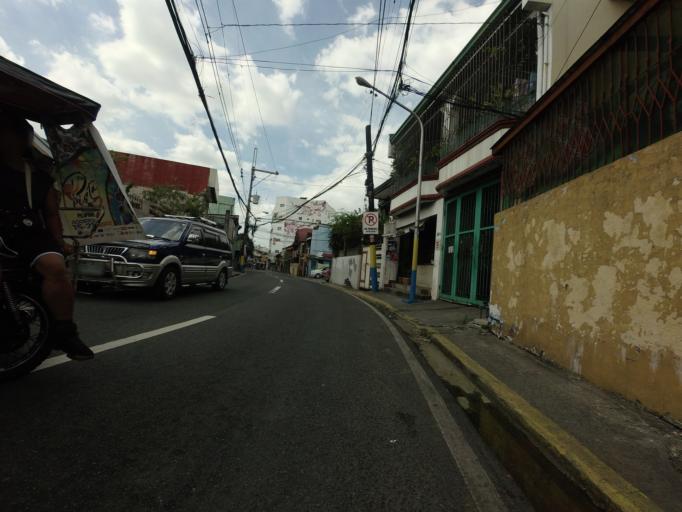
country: PH
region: Metro Manila
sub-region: Mandaluyong
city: Mandaluyong City
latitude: 14.5887
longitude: 121.0317
